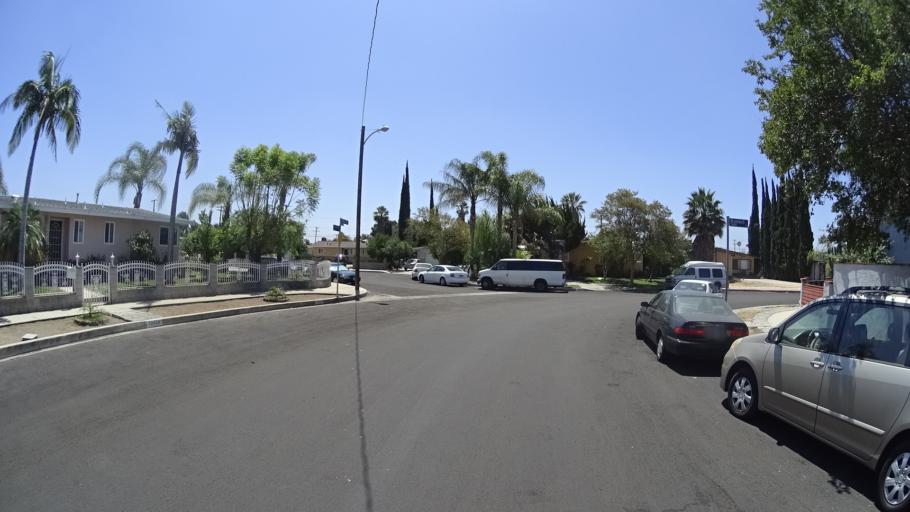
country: US
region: California
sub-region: Los Angeles County
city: San Fernando
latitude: 34.2385
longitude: -118.4260
